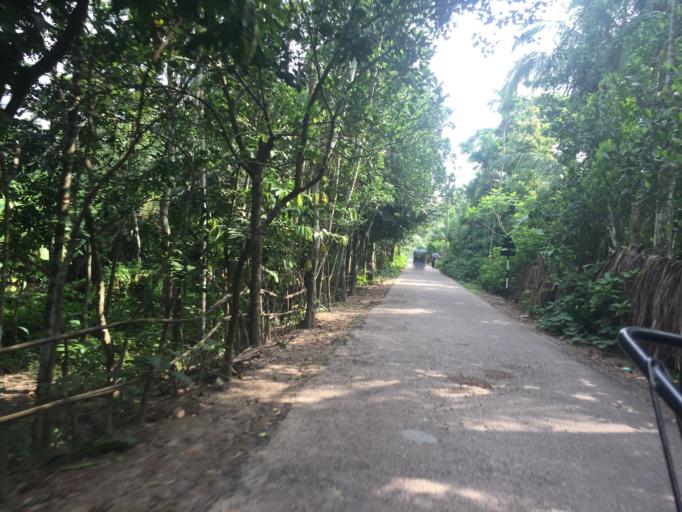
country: BD
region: Barisal
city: Mathba
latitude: 22.2184
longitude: 89.9159
